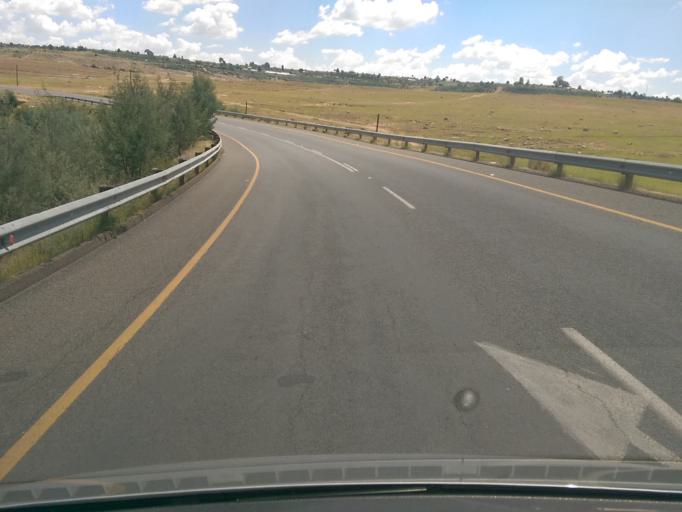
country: LS
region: Maseru
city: Maseru
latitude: -29.3903
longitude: 27.5504
